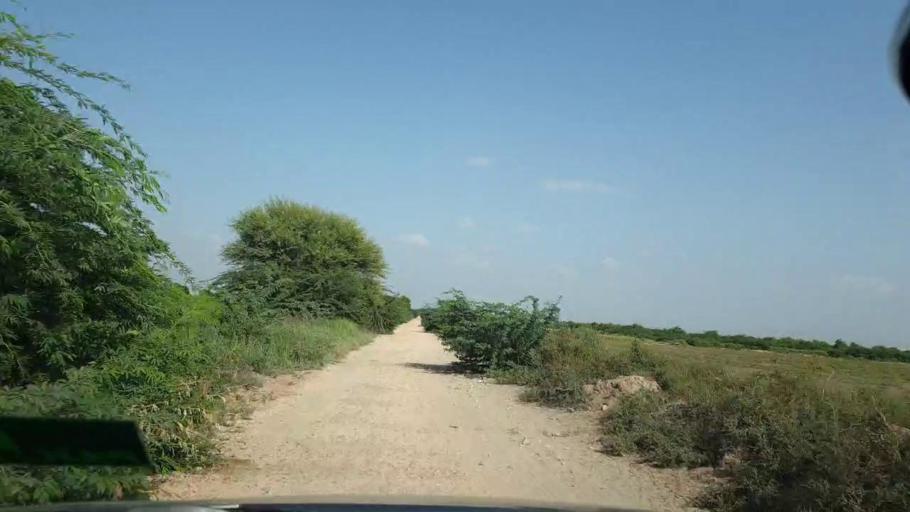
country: PK
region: Sindh
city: Naukot
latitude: 24.7031
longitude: 69.2057
